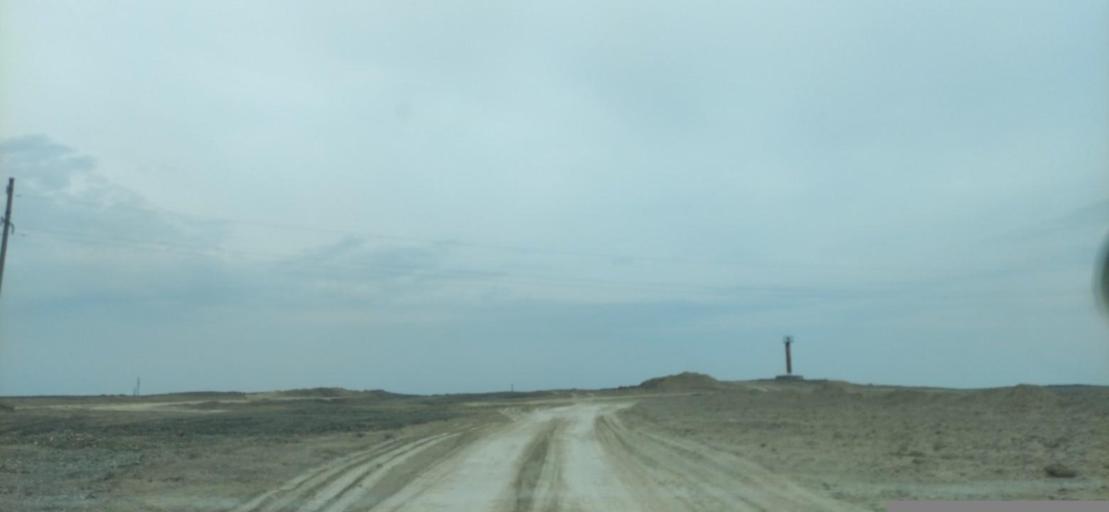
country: KZ
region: Qaraghandy
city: Saryshaghan
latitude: 46.0233
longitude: 73.5903
